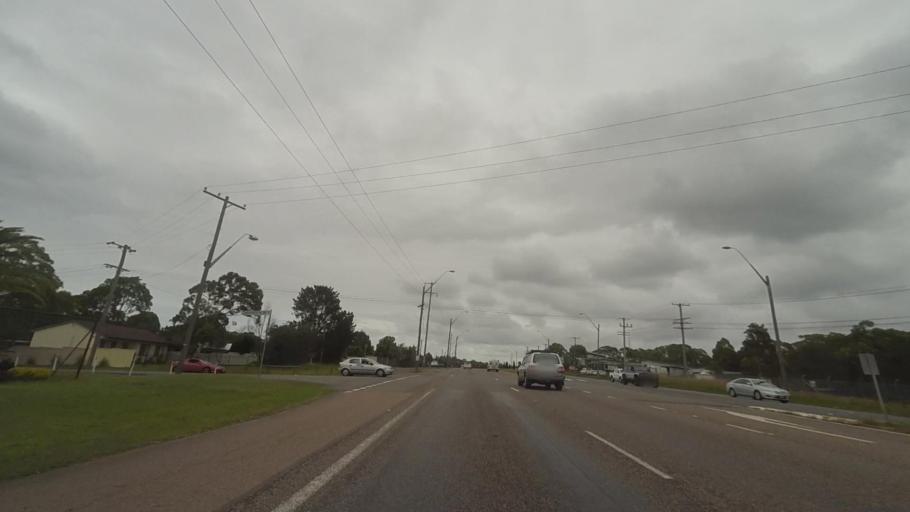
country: AU
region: New South Wales
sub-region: Wyong Shire
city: Buff Point
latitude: -33.1975
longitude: 151.5247
